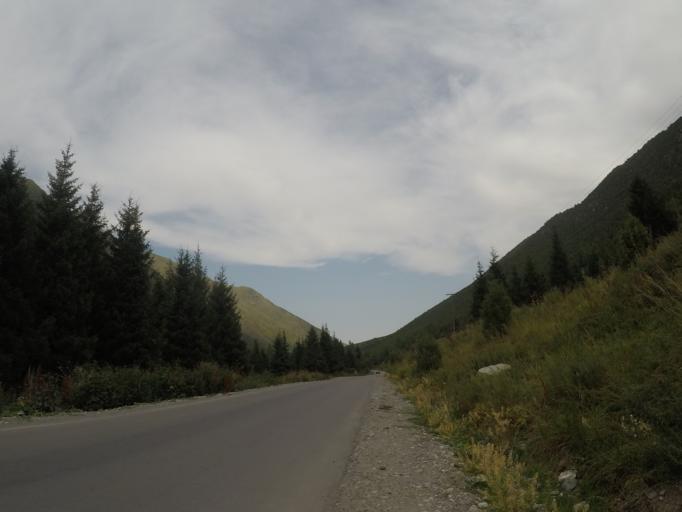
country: KG
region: Chuy
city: Bishkek
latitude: 42.5911
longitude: 74.4832
